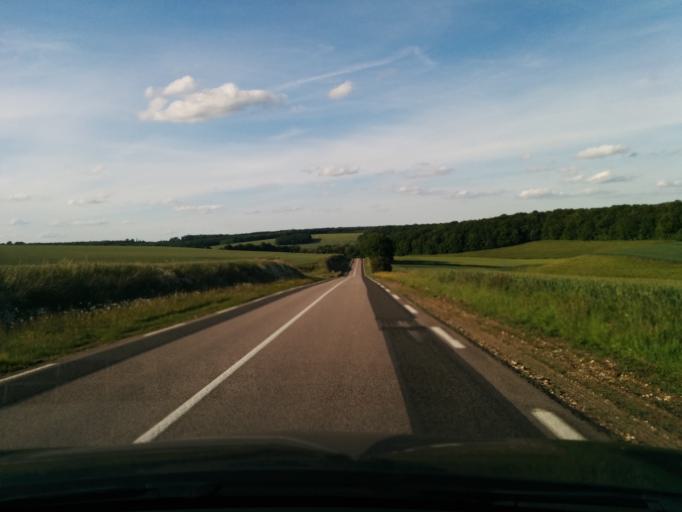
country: FR
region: Haute-Normandie
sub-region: Departement de l'Eure
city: Charleval
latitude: 49.3386
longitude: 1.4503
